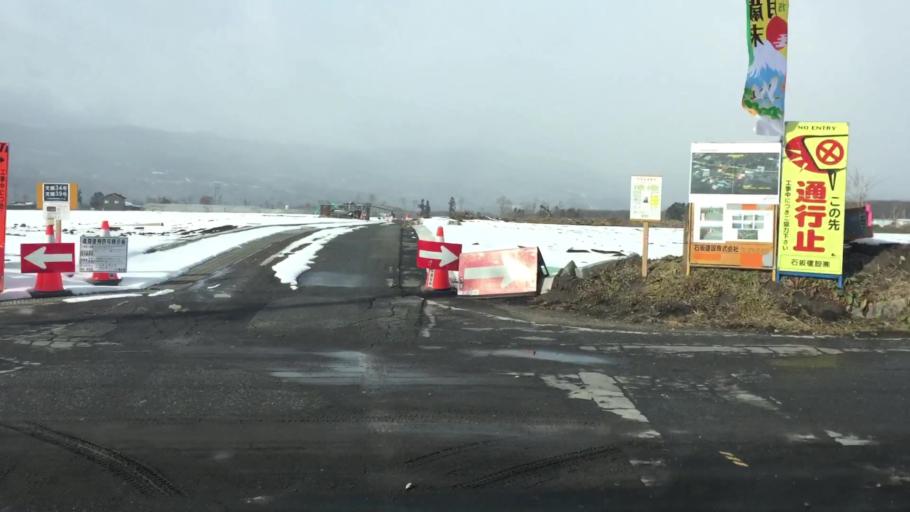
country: JP
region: Gunma
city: Numata
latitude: 36.6051
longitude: 139.0901
